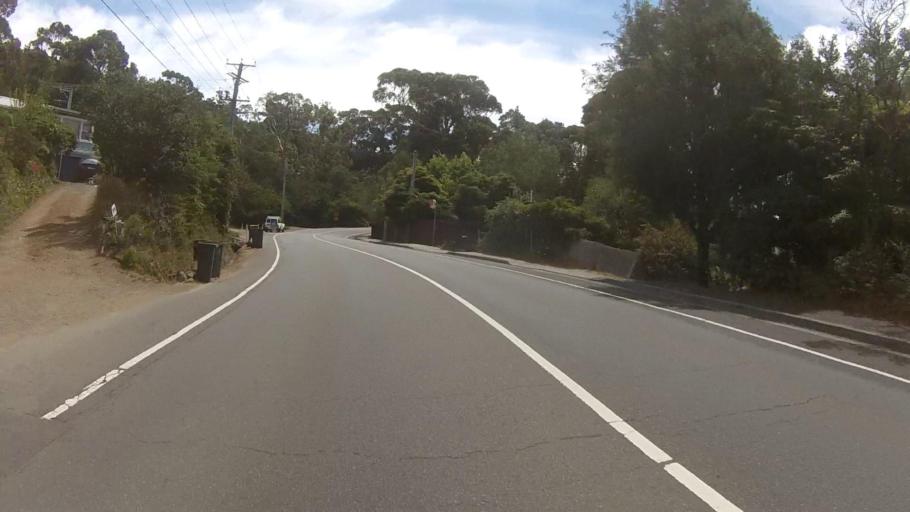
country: AU
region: Tasmania
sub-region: Kingborough
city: Taroona
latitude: -42.9380
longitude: 147.3531
